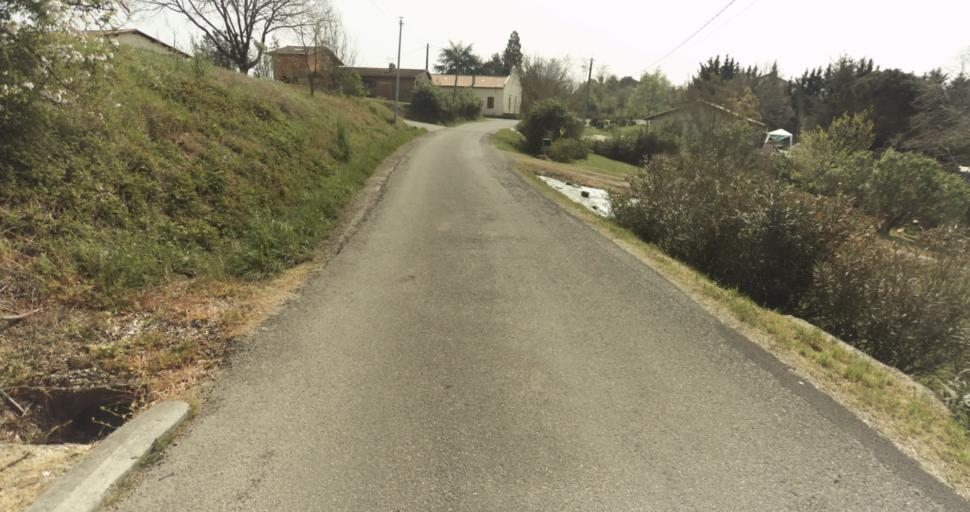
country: FR
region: Midi-Pyrenees
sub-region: Departement du Tarn-et-Garonne
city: Moissac
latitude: 44.1138
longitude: 1.0840
